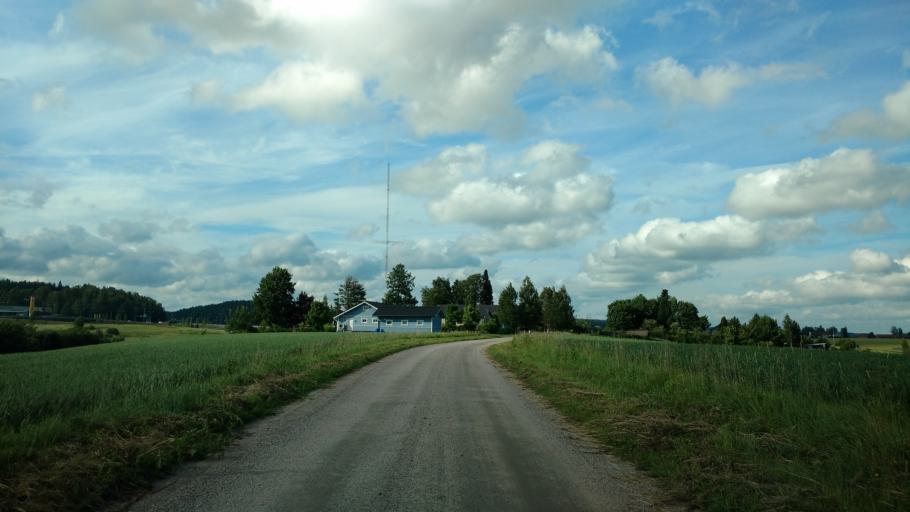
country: FI
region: Varsinais-Suomi
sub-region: Salo
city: Salo
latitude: 60.4120
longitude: 23.1684
